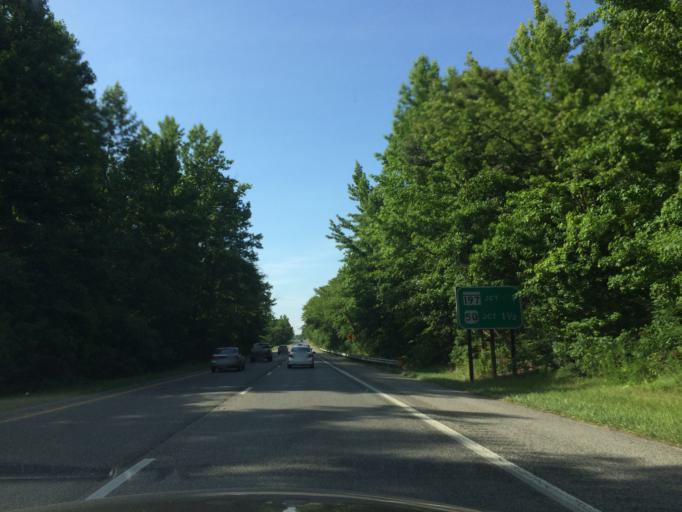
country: US
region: Maryland
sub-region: Prince George's County
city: Bowie
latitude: 38.9271
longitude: -76.7164
